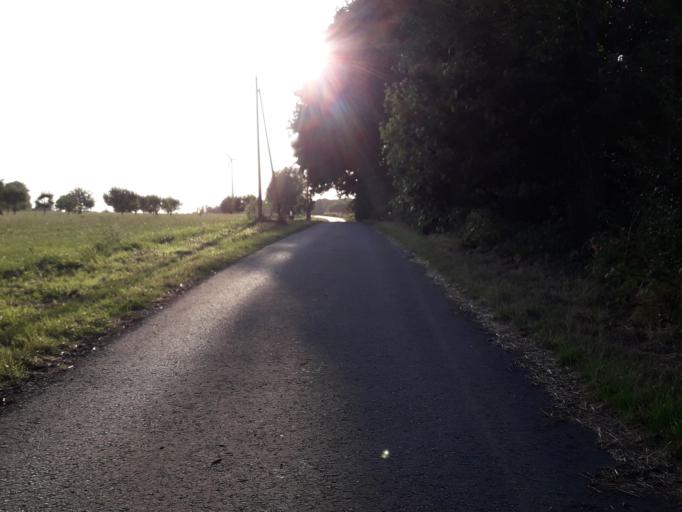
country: DE
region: North Rhine-Westphalia
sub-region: Regierungsbezirk Detmold
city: Paderborn
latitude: 51.7131
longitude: 8.6809
